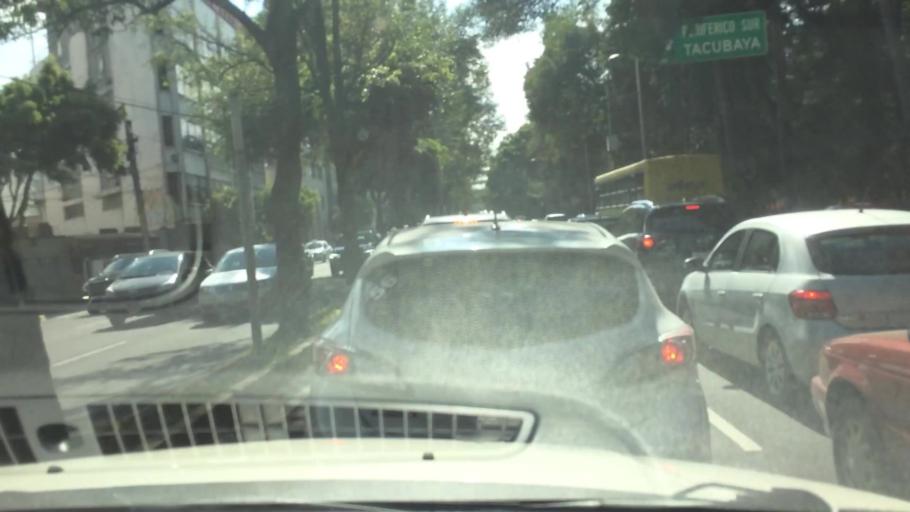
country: MX
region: Mexico City
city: Polanco
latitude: 19.4145
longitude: -99.1868
